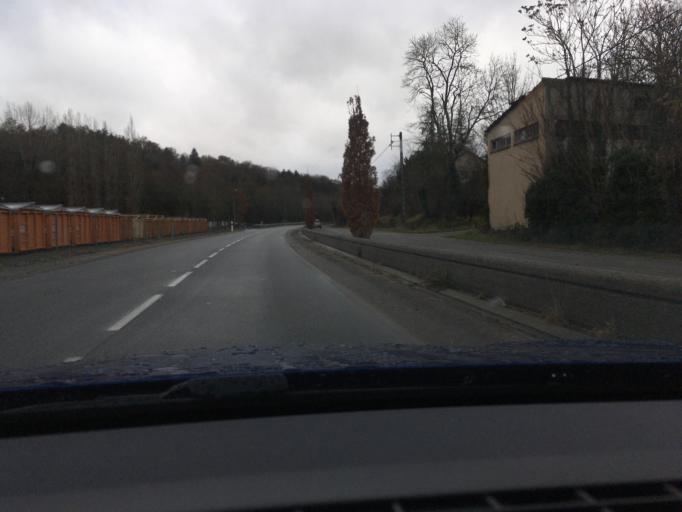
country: FR
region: Midi-Pyrenees
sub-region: Departement de l'Aveyron
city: Villefranche-de-Rouergue
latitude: 44.3656
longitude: 2.0169
